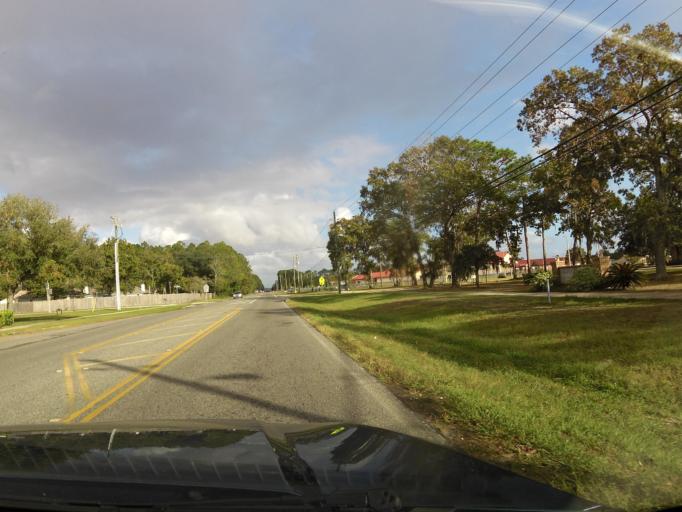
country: US
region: Florida
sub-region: Clay County
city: Asbury Lake
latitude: 30.0460
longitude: -81.8077
